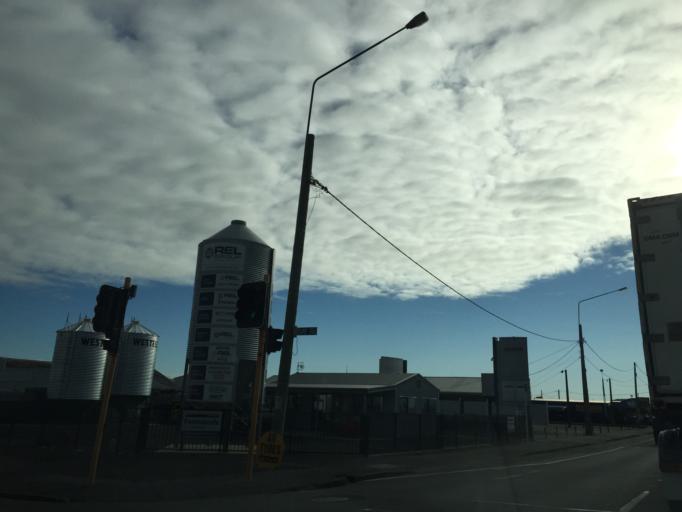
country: NZ
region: Southland
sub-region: Invercargill City
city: Invercargill
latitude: -46.3892
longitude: 168.3473
